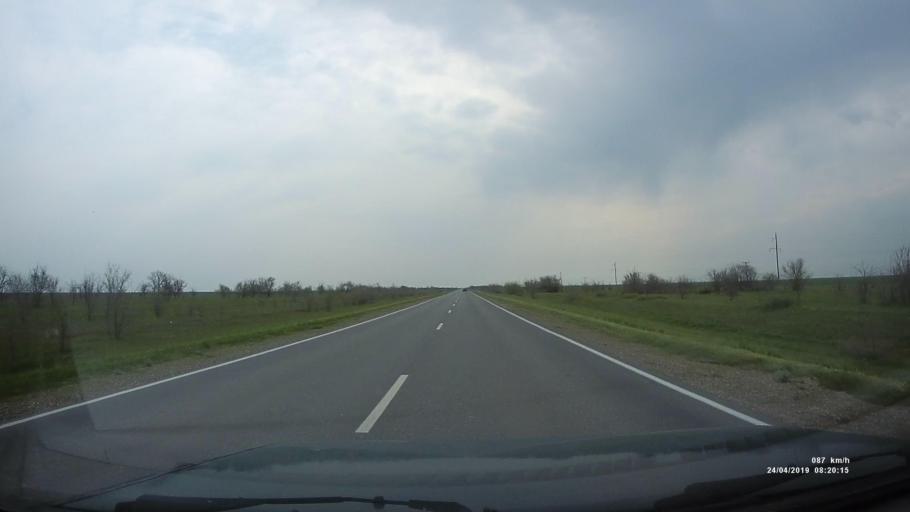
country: RU
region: Kalmykiya
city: Priyutnoye
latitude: 46.1067
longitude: 43.6795
